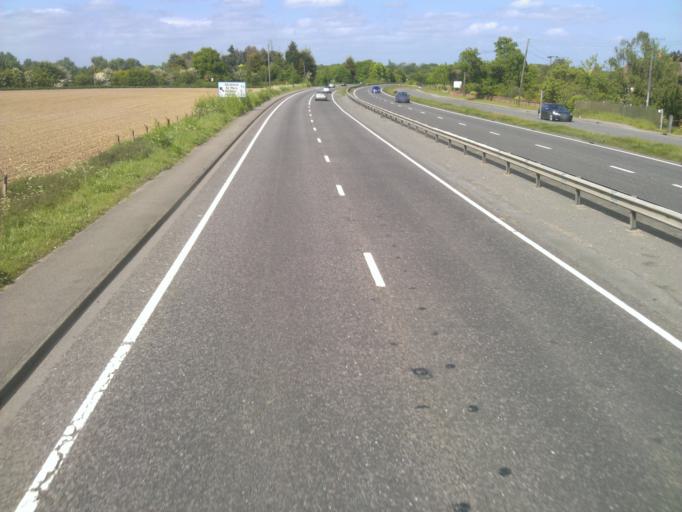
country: GB
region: England
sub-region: Suffolk
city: East Bergholt
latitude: 51.9500
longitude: 0.9598
